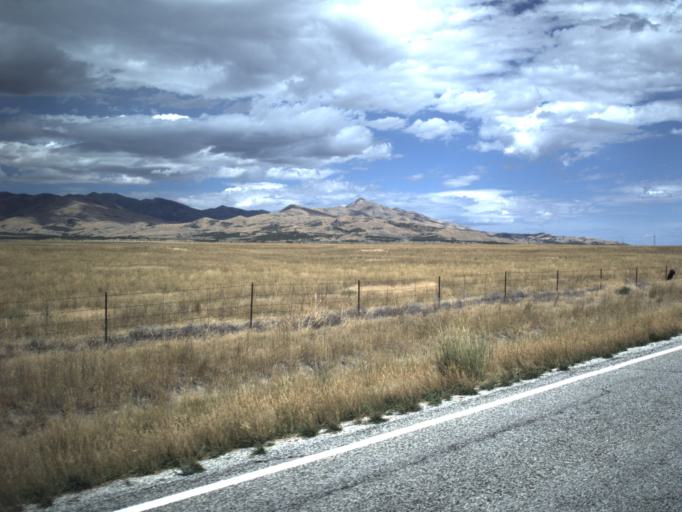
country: US
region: Idaho
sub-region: Oneida County
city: Malad City
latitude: 41.9554
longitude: -113.0720
